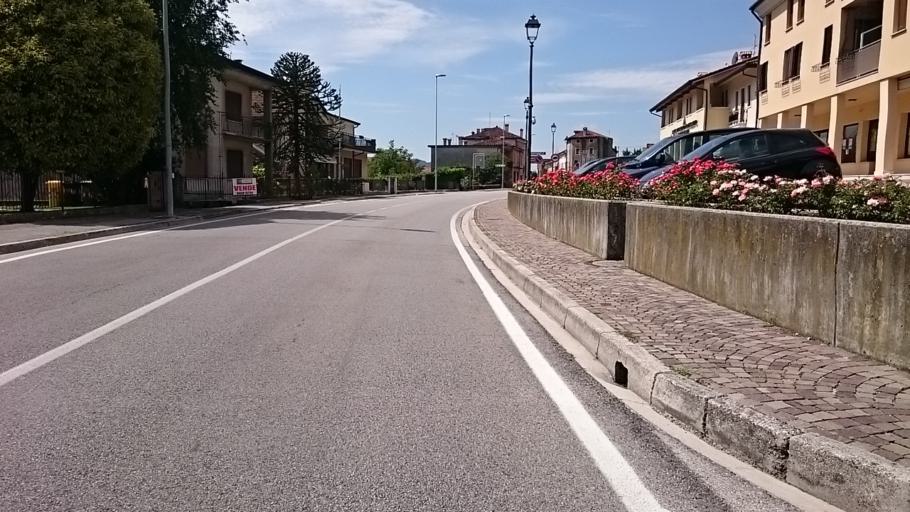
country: IT
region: Veneto
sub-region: Provincia di Treviso
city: Revine
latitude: 46.0000
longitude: 12.2568
